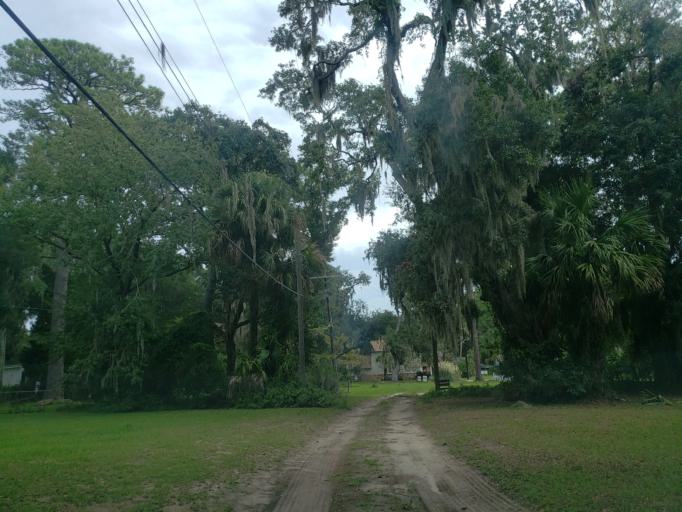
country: US
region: Georgia
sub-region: Chatham County
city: Wilmington Island
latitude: 31.9768
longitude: -80.9969
